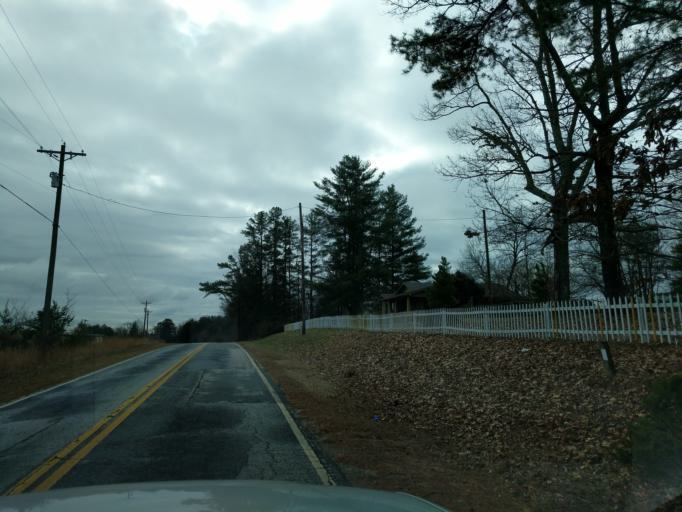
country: US
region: Georgia
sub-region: Rabun County
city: Clayton
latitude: 34.7880
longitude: -83.2497
